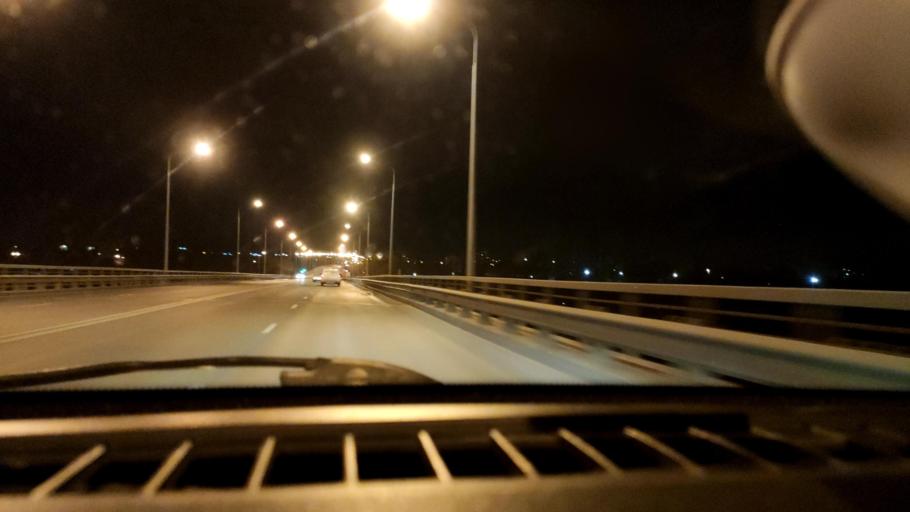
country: RU
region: Samara
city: Samara
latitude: 53.1686
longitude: 50.1960
